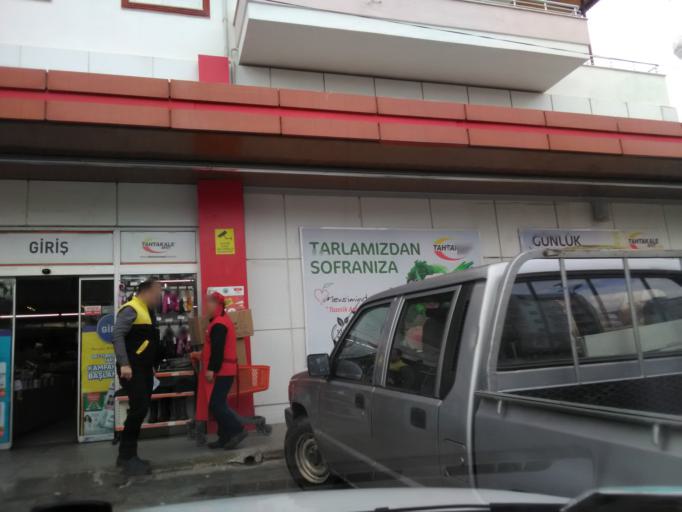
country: TR
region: Antalya
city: Gazipasa
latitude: 36.2770
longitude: 32.3160
